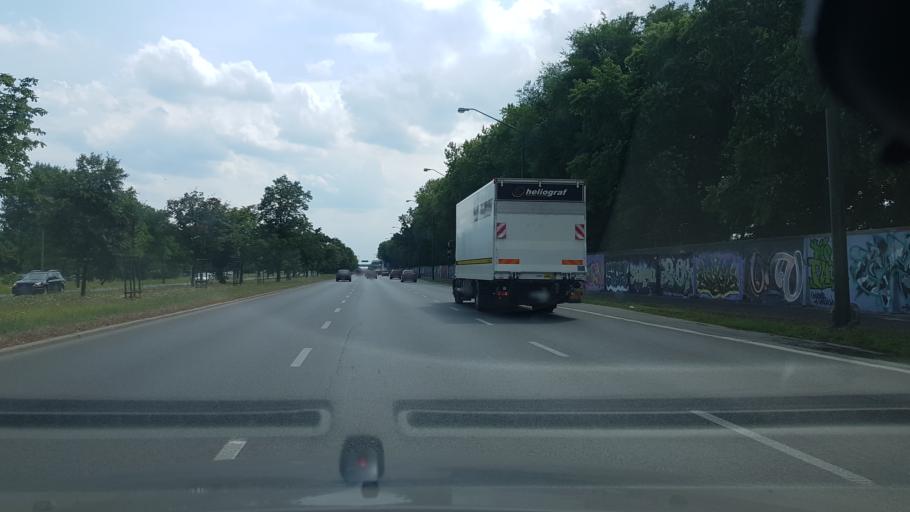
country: PL
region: Masovian Voivodeship
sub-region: Warszawa
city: Ursynow
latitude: 52.1606
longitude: 21.0173
